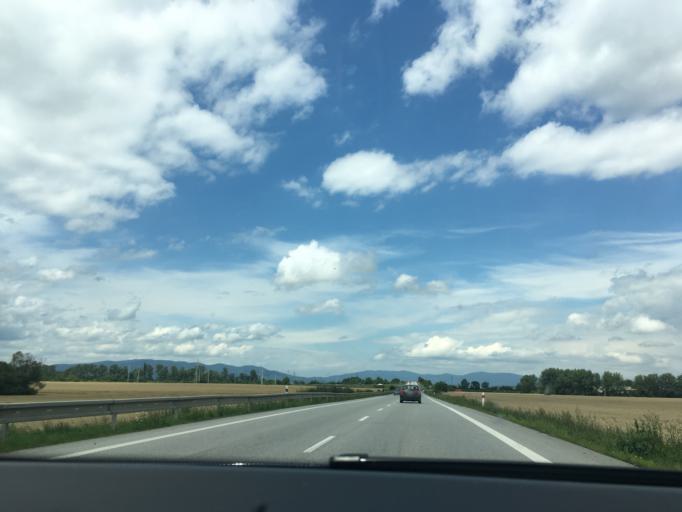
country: SK
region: Kosicky
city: Trebisov
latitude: 48.6197
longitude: 21.7027
